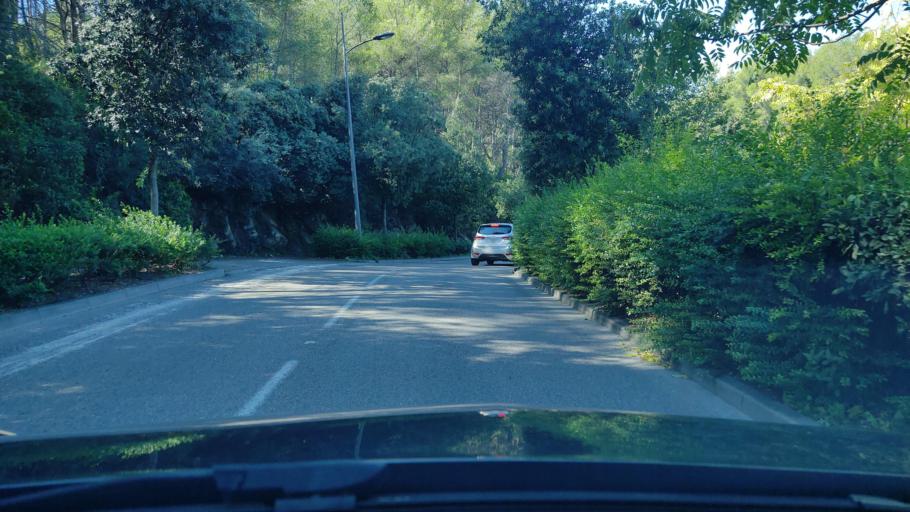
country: FR
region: Provence-Alpes-Cote d'Azur
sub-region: Departement du Var
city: Sanary-sur-Mer
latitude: 43.1443
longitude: 5.7720
